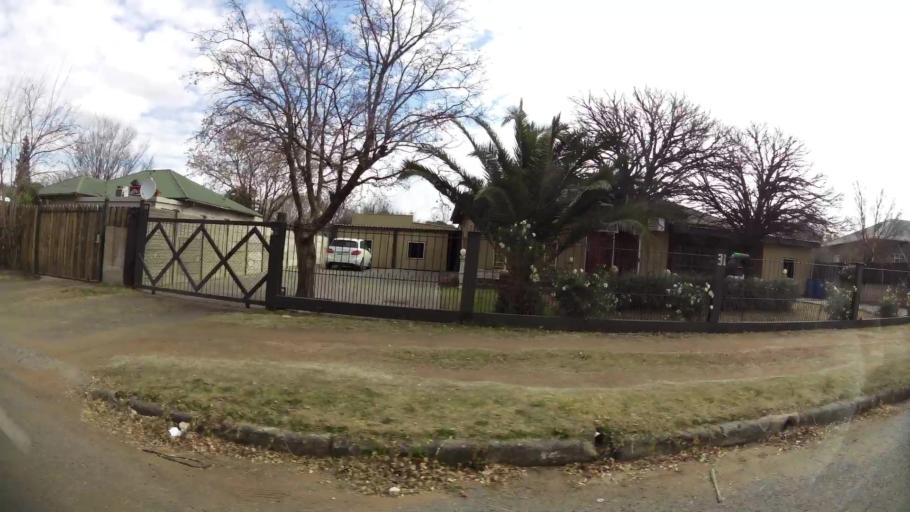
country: ZA
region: Orange Free State
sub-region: Mangaung Metropolitan Municipality
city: Bloemfontein
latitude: -29.0862
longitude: 26.2507
